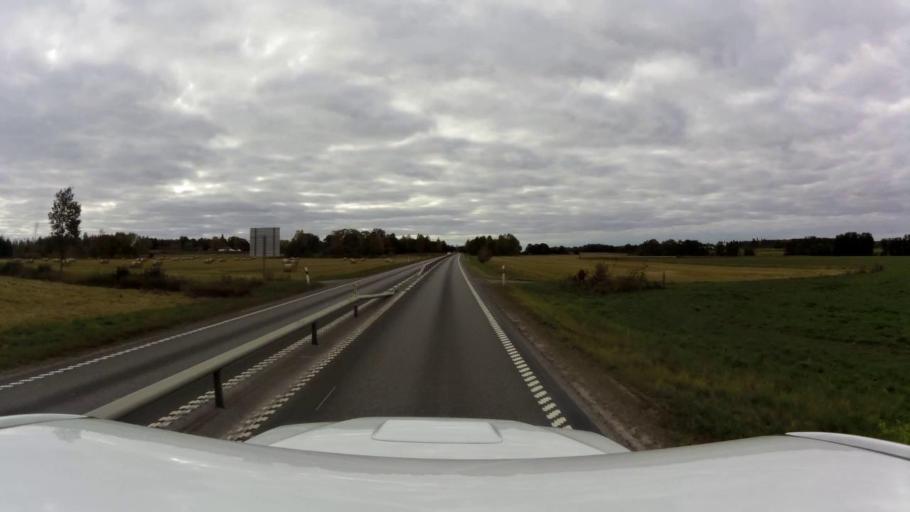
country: SE
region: OEstergoetland
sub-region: Linkopings Kommun
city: Malmslatt
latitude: 58.3688
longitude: 15.5441
